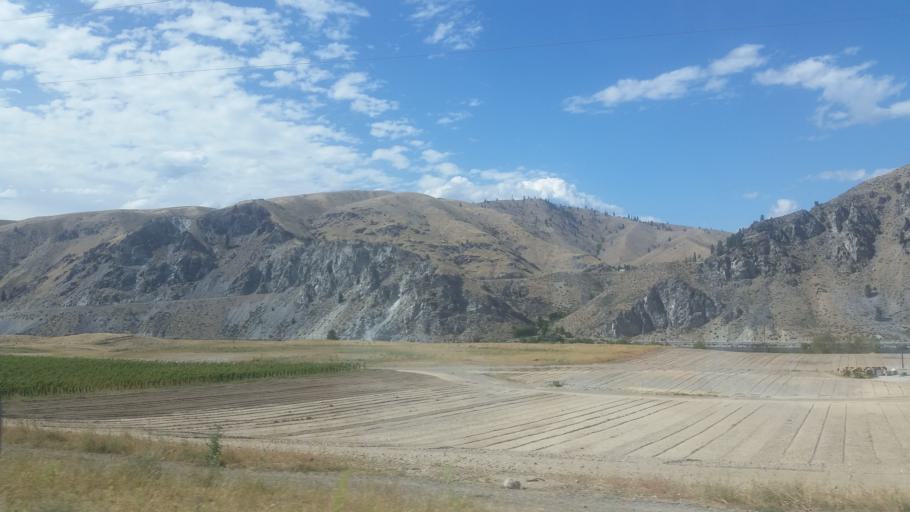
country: US
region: Washington
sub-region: Chelan County
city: Entiat
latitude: 47.7675
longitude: -120.1333
